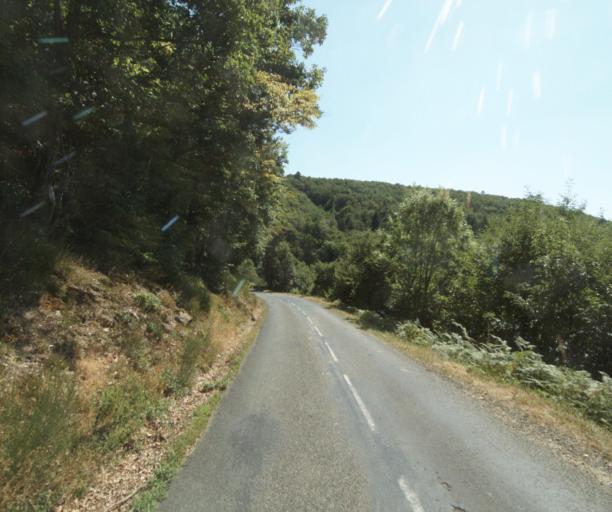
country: FR
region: Rhone-Alpes
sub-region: Departement du Rhone
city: Courzieu
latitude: 45.7207
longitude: 4.5493
